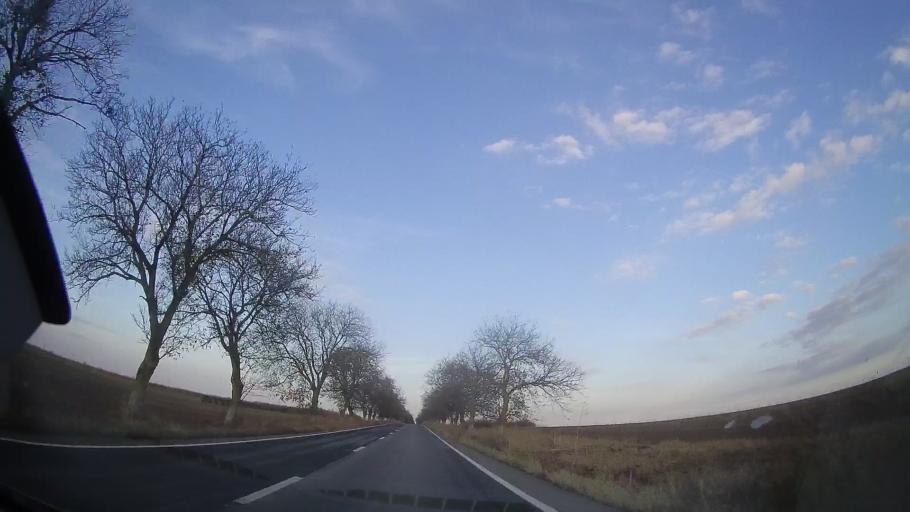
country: RO
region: Constanta
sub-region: Comuna Chirnogeni
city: Chirnogeni
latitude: 43.8613
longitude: 28.2590
